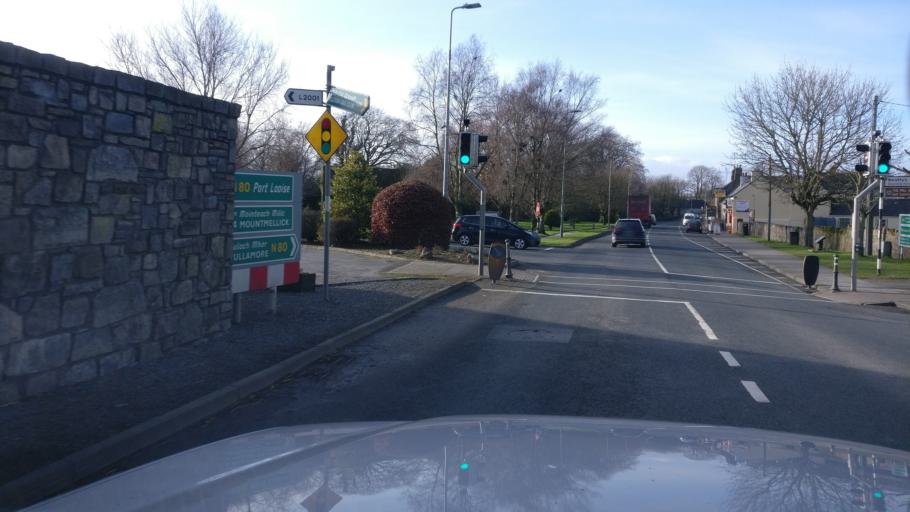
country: IE
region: Leinster
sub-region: Uibh Fhaili
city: Tullamore
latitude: 53.2140
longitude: -7.4495
